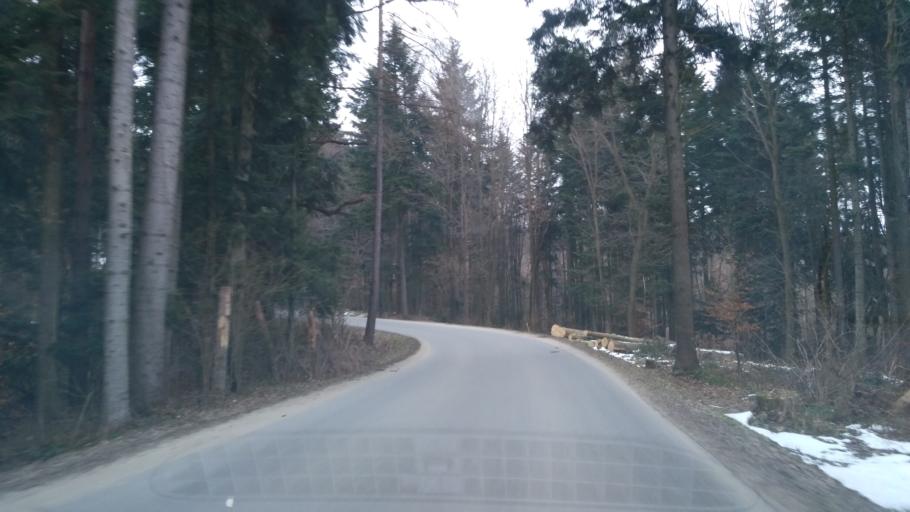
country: PL
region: Subcarpathian Voivodeship
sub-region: Powiat strzyzowski
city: Polomia
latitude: 49.9050
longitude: 21.8966
